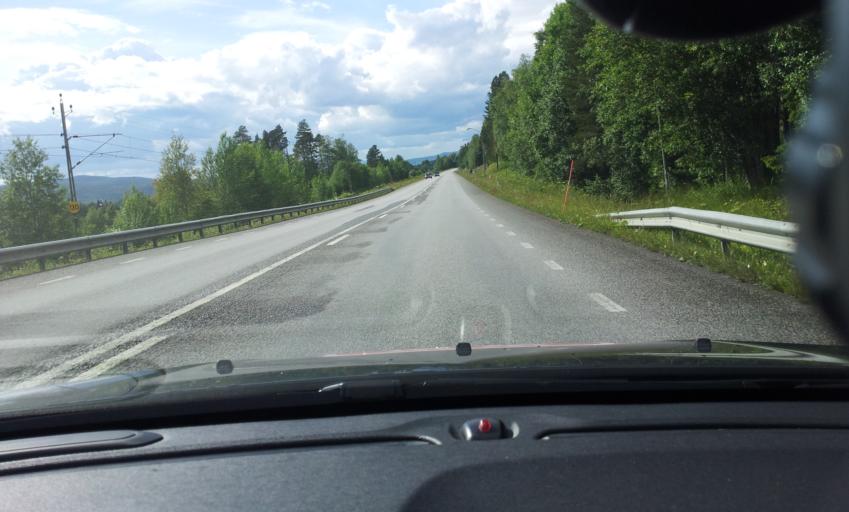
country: SE
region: Jaemtland
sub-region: Are Kommun
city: Jarpen
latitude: 63.3087
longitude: 13.6201
